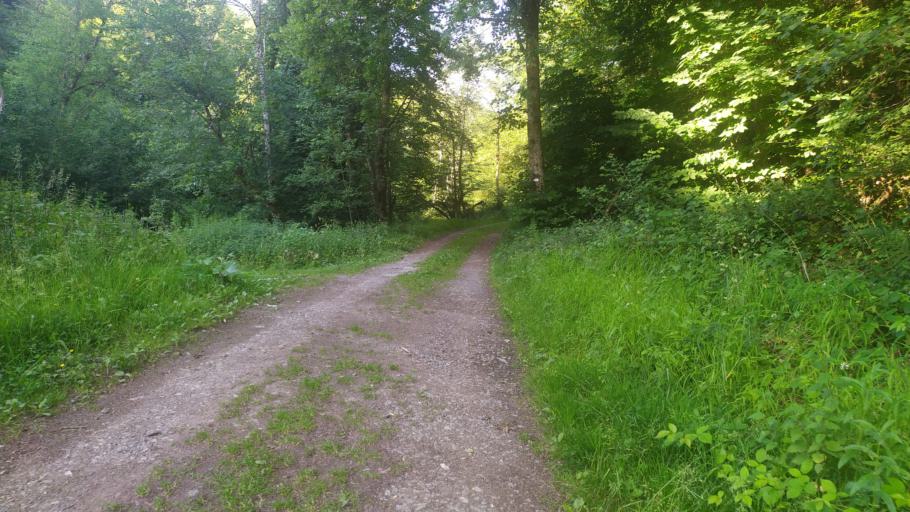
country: BE
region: Wallonia
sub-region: Province de Namur
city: Houyet
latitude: 50.2027
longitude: 4.9983
